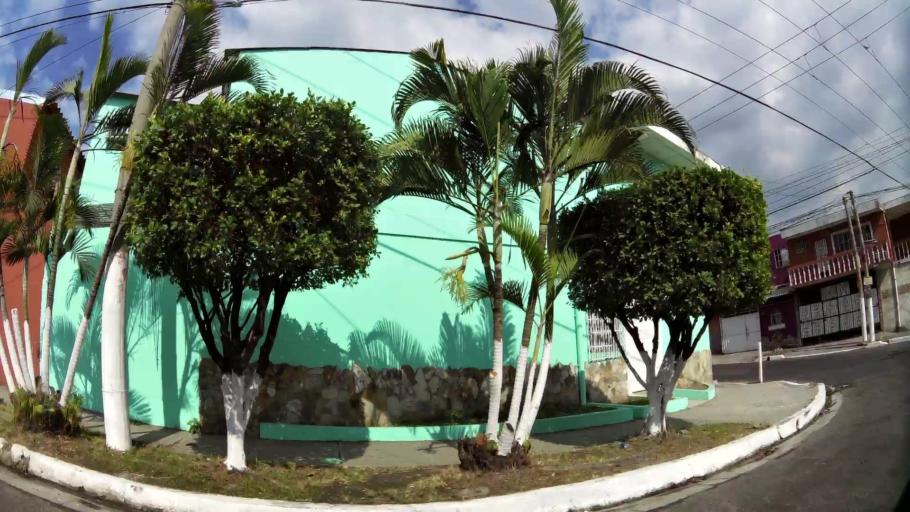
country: SV
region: San Salvador
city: Mejicanos
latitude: 13.7329
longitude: -89.2087
